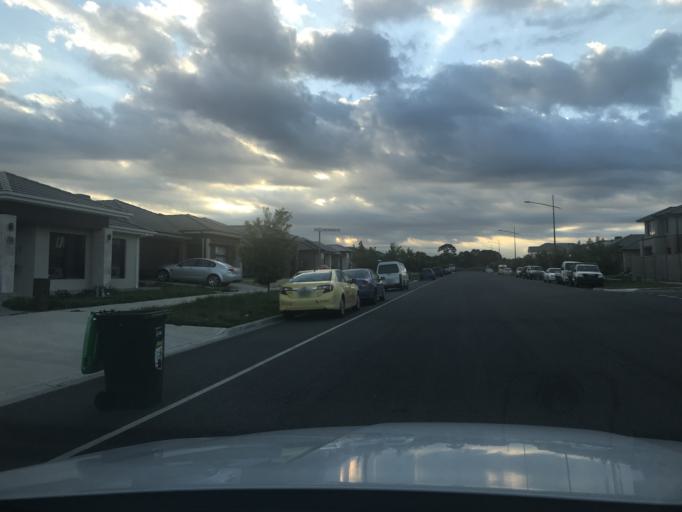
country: AU
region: Victoria
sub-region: Hume
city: Roxburgh Park
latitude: -37.5731
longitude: 144.8916
